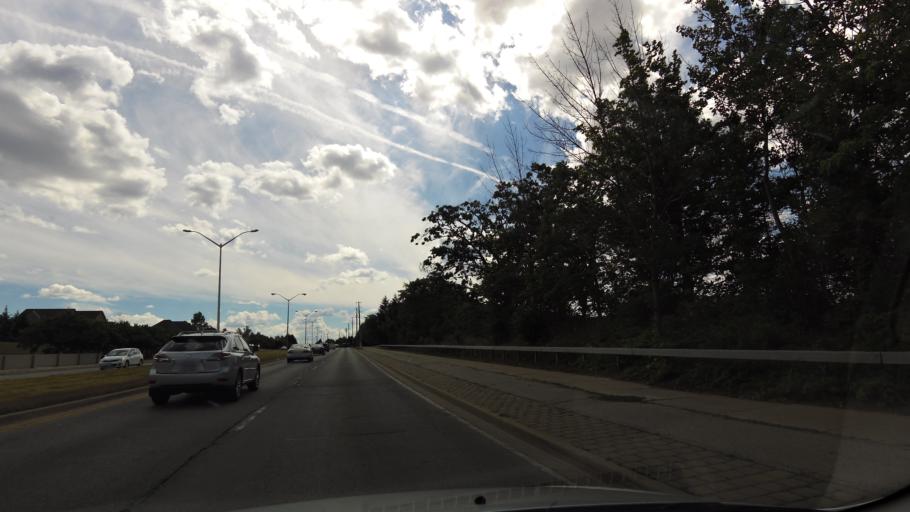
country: CA
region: Ontario
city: Oakville
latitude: 43.4536
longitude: -79.7245
